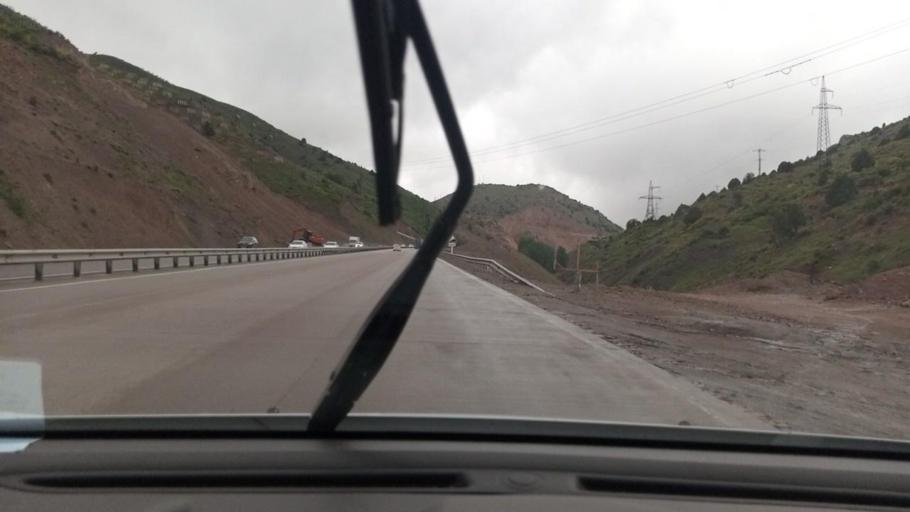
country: UZ
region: Toshkent
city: Angren
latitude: 41.0576
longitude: 70.5630
